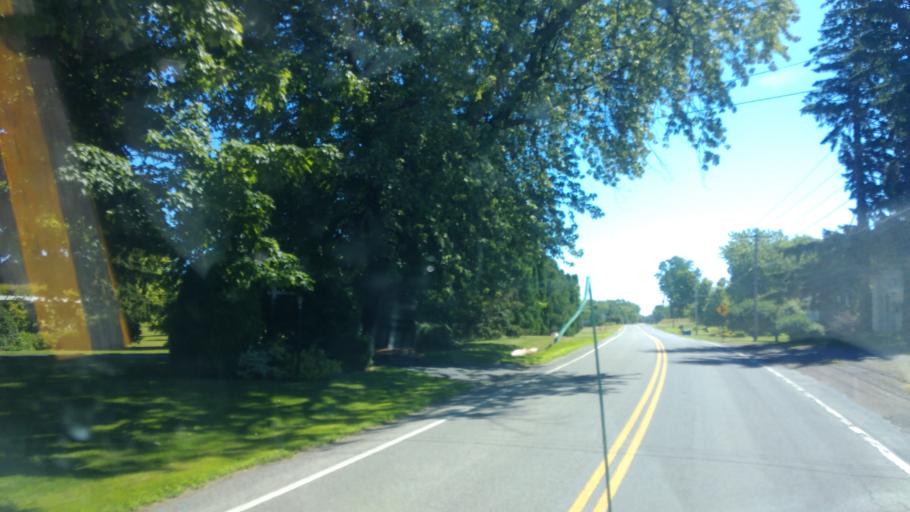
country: US
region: New York
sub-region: Wayne County
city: Williamson
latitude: 43.2803
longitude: -77.1666
